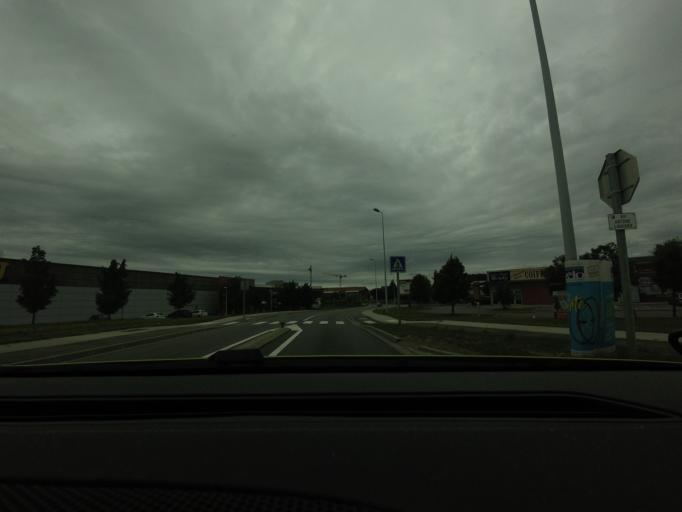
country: FR
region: Midi-Pyrenees
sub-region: Departement de la Haute-Garonne
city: Colomiers
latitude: 43.6111
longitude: 1.3084
